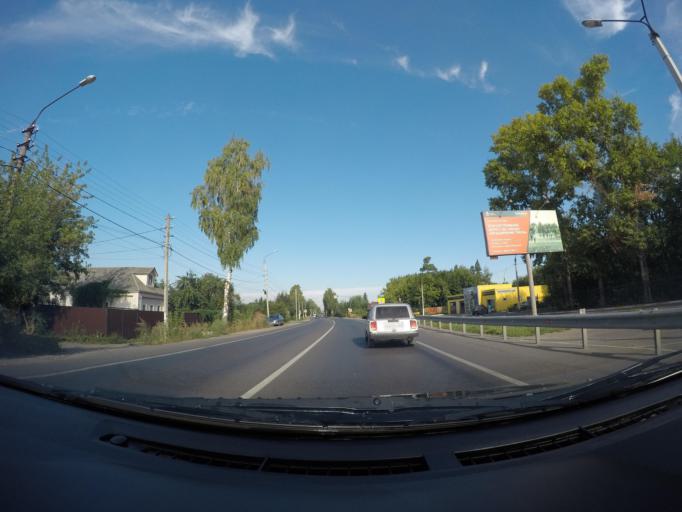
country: RU
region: Moskovskaya
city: Rechitsy
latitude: 55.5944
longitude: 38.4858
